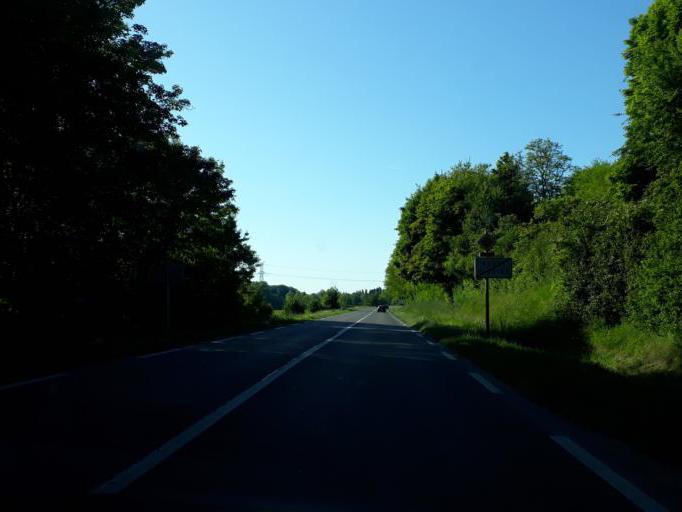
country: FR
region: Bourgogne
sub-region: Departement de la Nievre
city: Neuvy-sur-Loire
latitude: 47.5260
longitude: 2.8714
